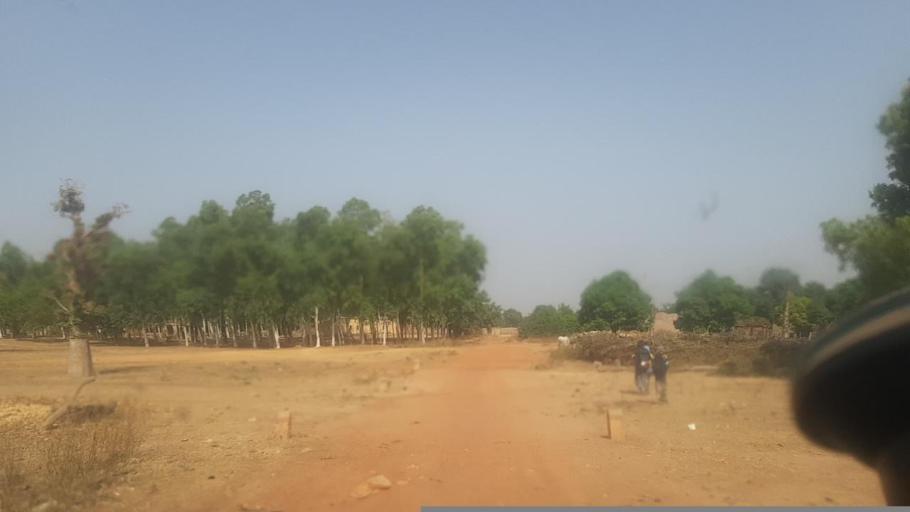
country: ML
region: Segou
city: Bla
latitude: 12.8483
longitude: -5.9906
